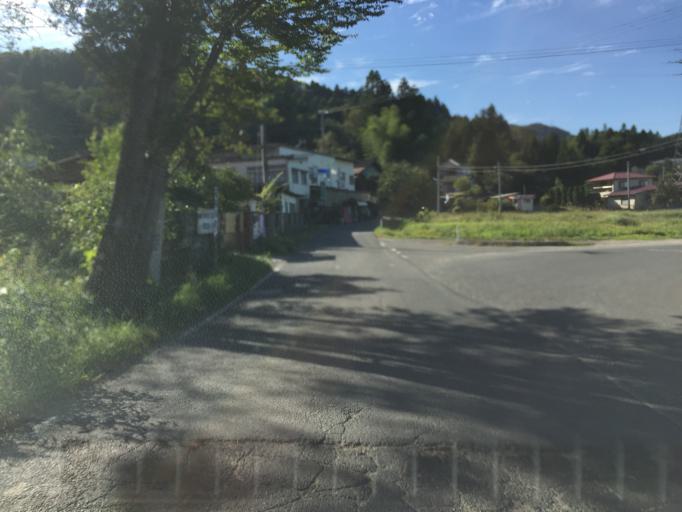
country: JP
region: Miyagi
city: Marumori
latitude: 37.9005
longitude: 140.7680
